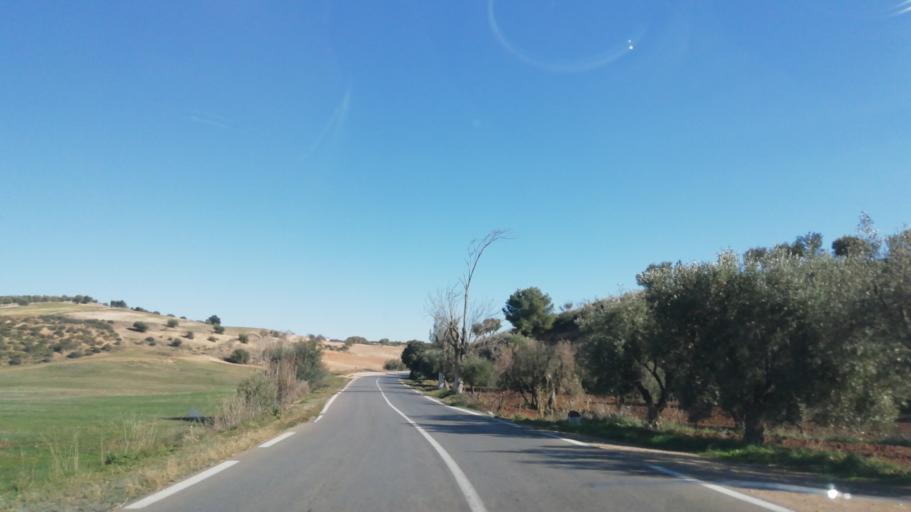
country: DZ
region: Tlemcen
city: Beni Mester
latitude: 34.8261
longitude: -1.5764
